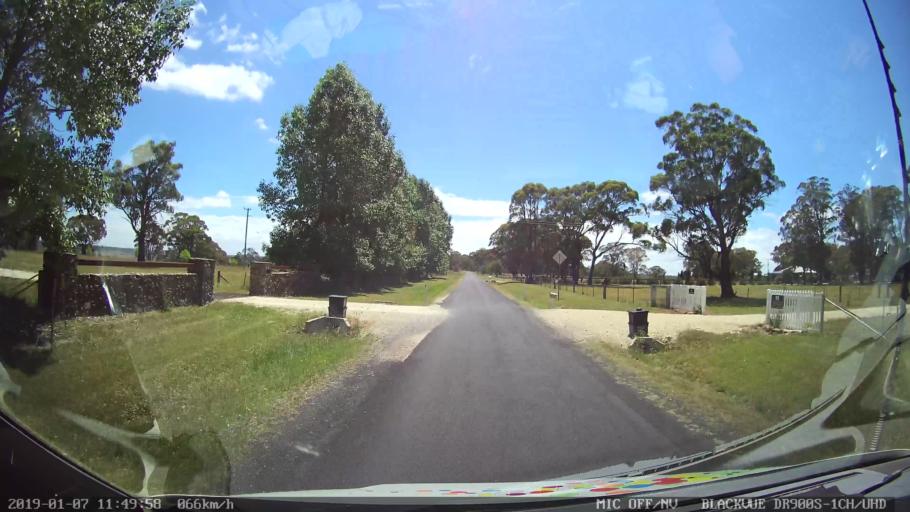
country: AU
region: New South Wales
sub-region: Guyra
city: Guyra
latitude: -30.3145
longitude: 151.6313
